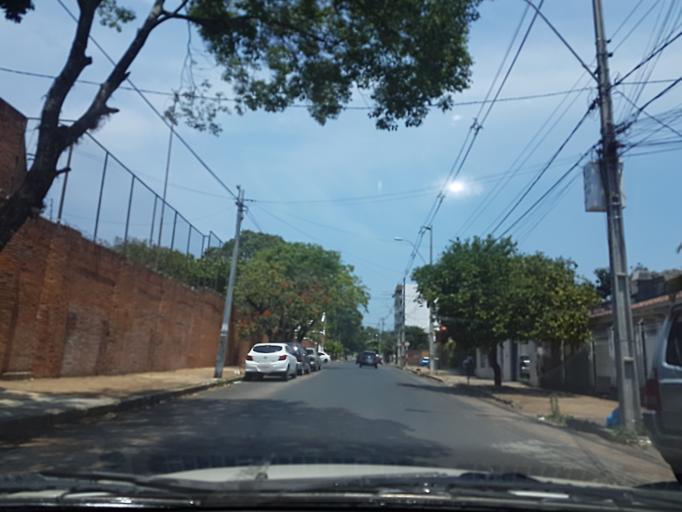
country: PY
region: Asuncion
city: Asuncion
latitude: -25.2905
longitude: -57.6066
